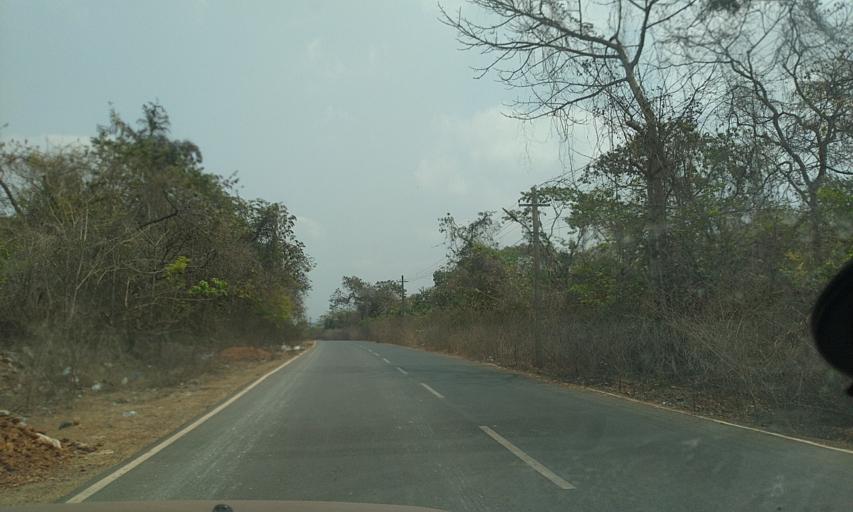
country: IN
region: Goa
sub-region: North Goa
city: Goa Velha
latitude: 15.4877
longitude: 73.9105
